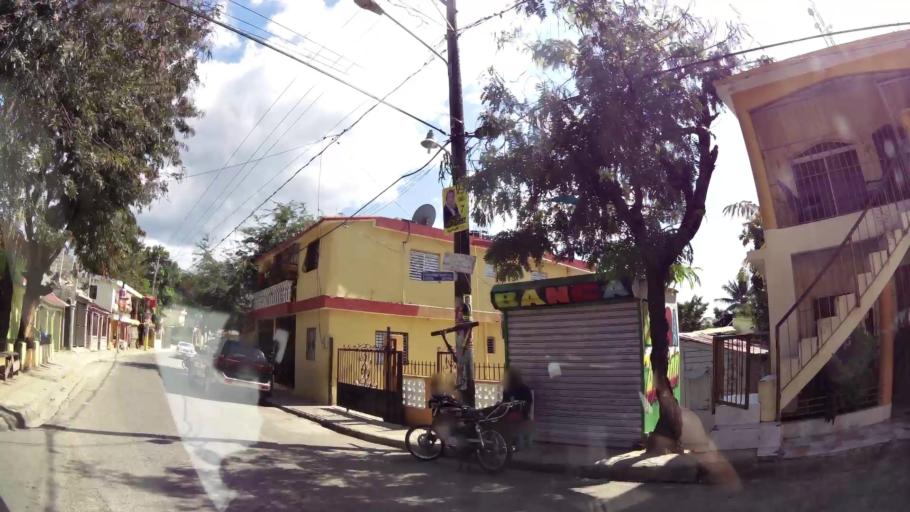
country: DO
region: San Cristobal
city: San Cristobal
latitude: 18.4233
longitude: -70.0823
